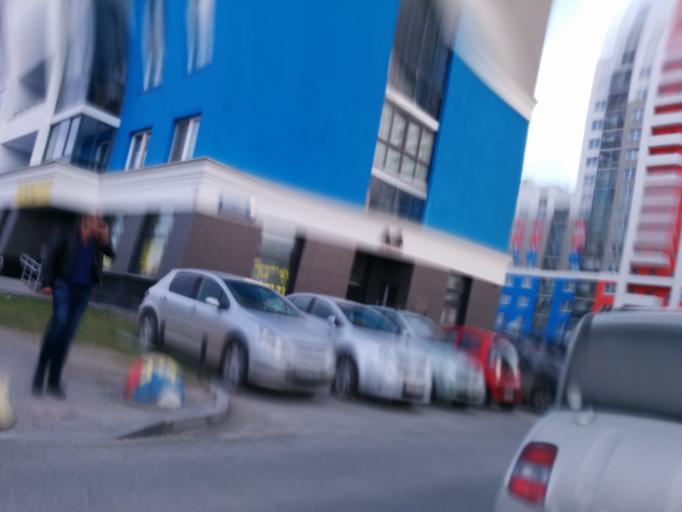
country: RU
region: Sverdlovsk
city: Shirokaya Rechka
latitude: 56.7948
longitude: 60.5179
